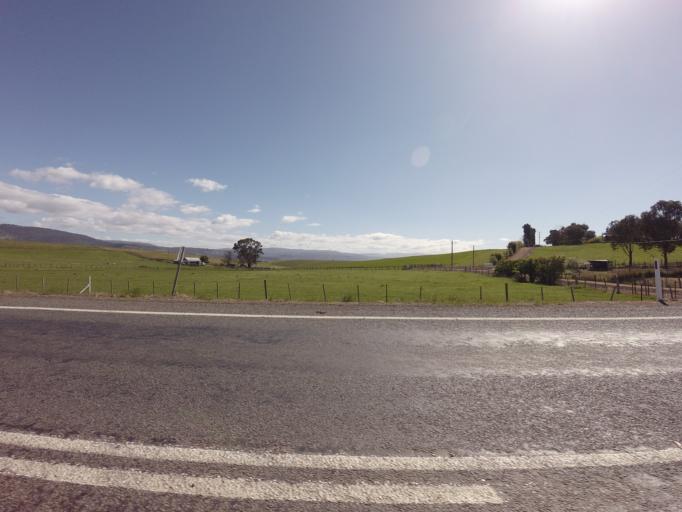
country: AU
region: Tasmania
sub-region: Derwent Valley
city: New Norfolk
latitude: -42.7018
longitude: 146.9419
